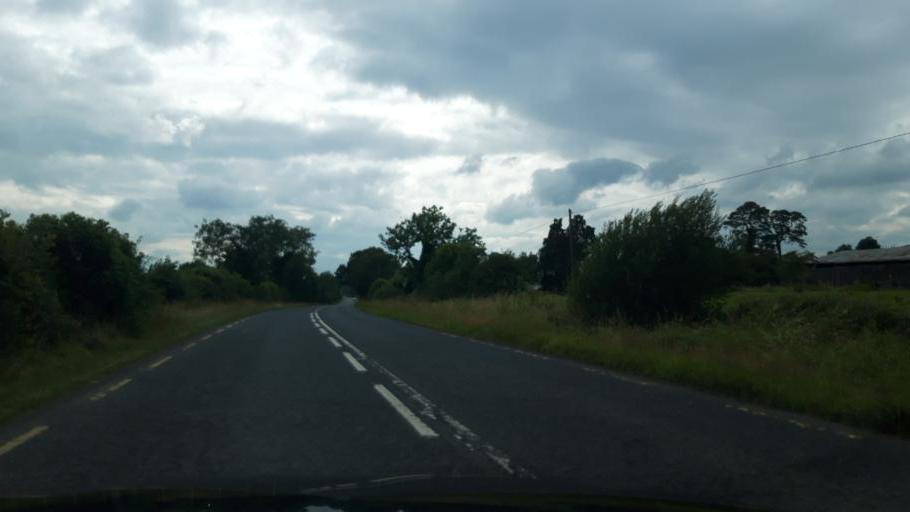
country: IE
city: Ballylinan
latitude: 52.8745
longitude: -7.0890
